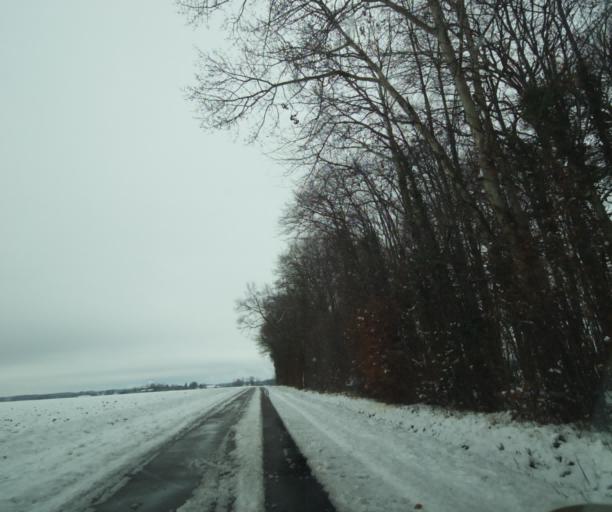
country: FR
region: Champagne-Ardenne
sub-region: Departement de la Haute-Marne
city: Montier-en-Der
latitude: 48.4637
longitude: 4.6519
